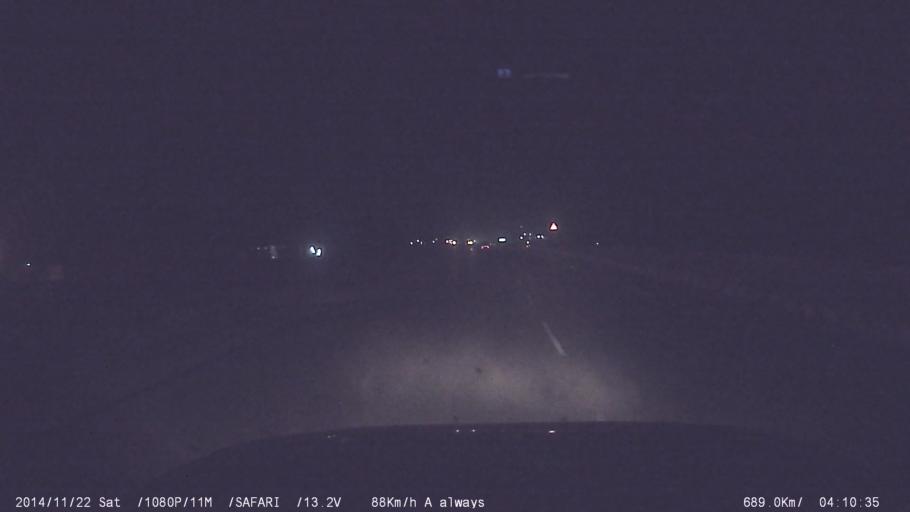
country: IN
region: Tamil Nadu
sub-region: Erode
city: Vijayapuri
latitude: 11.2533
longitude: 77.5432
